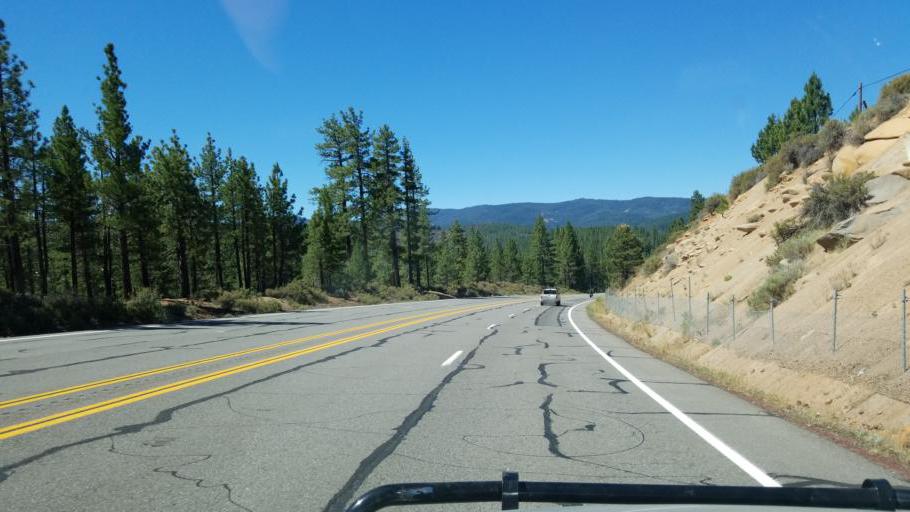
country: US
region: California
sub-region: Lassen County
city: Susanville
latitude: 40.4020
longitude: -120.7712
